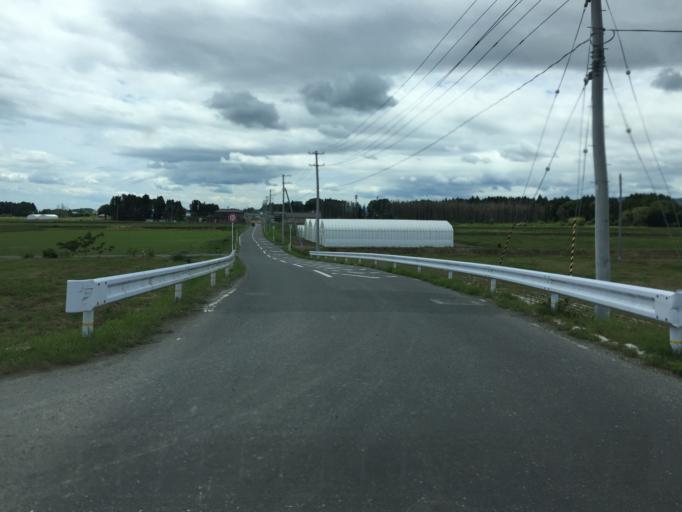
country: JP
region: Fukushima
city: Namie
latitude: 37.6437
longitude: 141.0019
